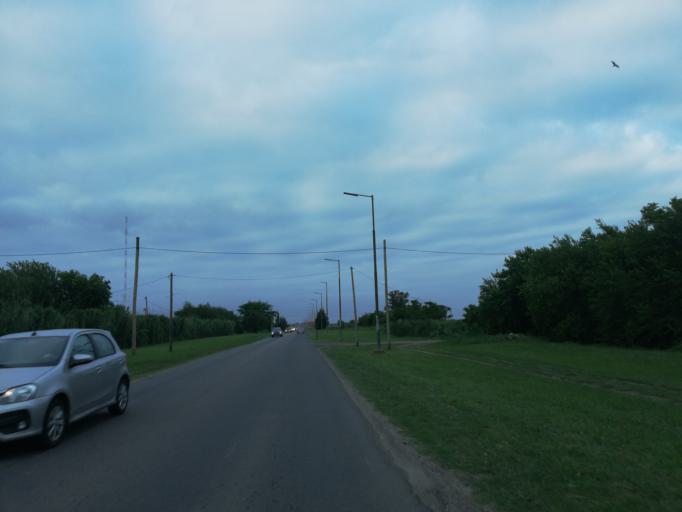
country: AR
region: Buenos Aires
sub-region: Partido de La Plata
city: La Plata
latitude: -34.8452
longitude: -58.0761
